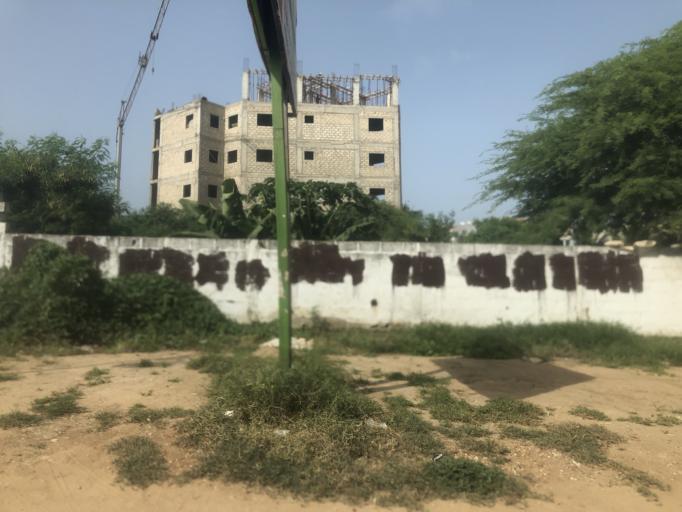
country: SN
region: Dakar
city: Mermoz Boabab
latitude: 14.7374
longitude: -17.5106
